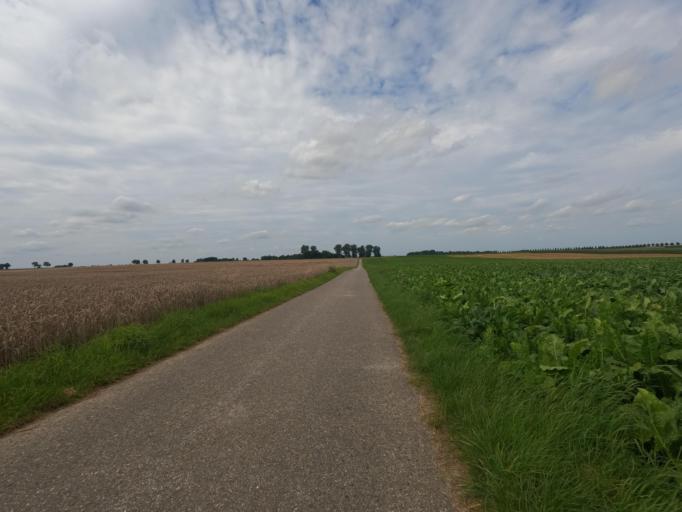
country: DE
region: North Rhine-Westphalia
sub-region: Regierungsbezirk Koln
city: Ubach-Palenberg
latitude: 50.9366
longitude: 6.1458
